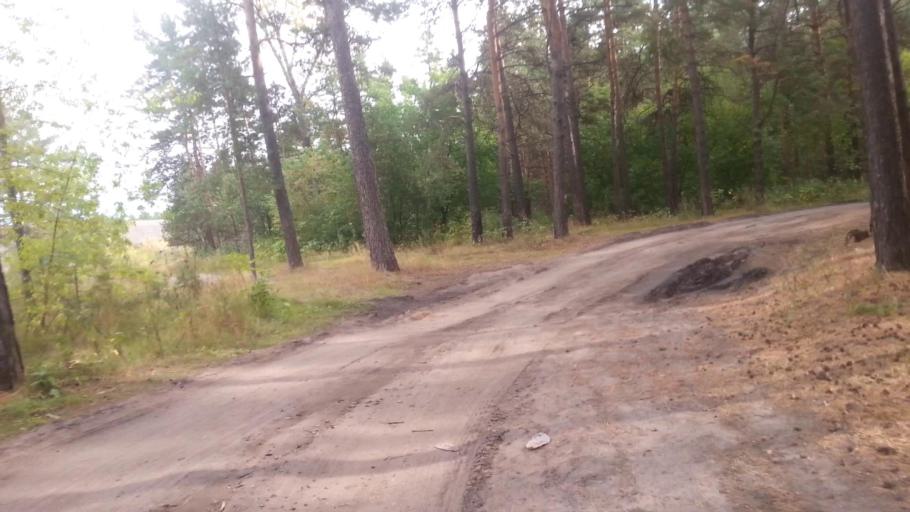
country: RU
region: Altai Krai
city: Yuzhnyy
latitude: 53.3104
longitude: 83.6990
